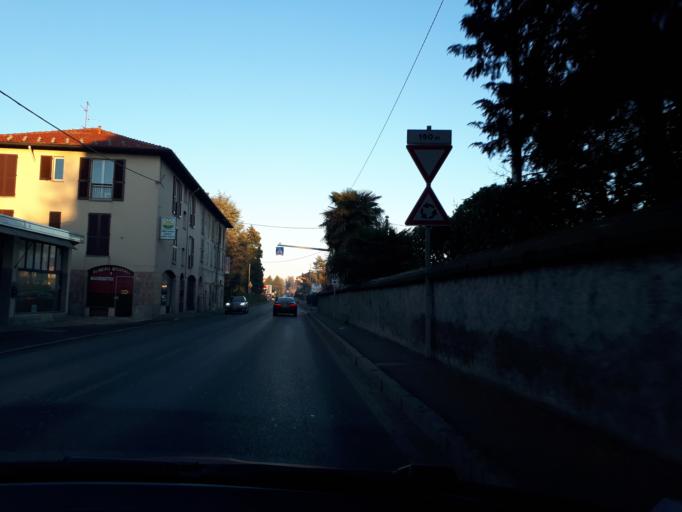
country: IT
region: Lombardy
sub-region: Provincia di Como
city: Cermenate
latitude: 45.7030
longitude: 9.0926
